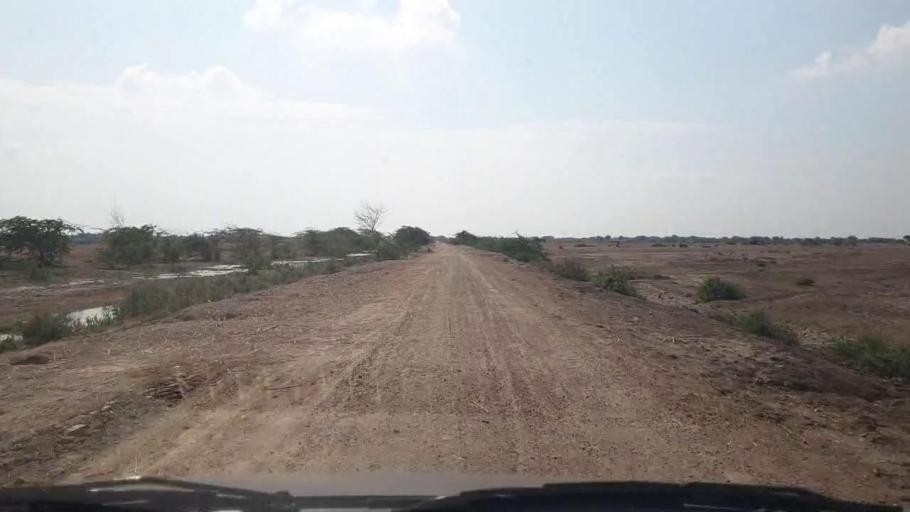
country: PK
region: Sindh
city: Badin
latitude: 24.4945
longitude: 68.6119
